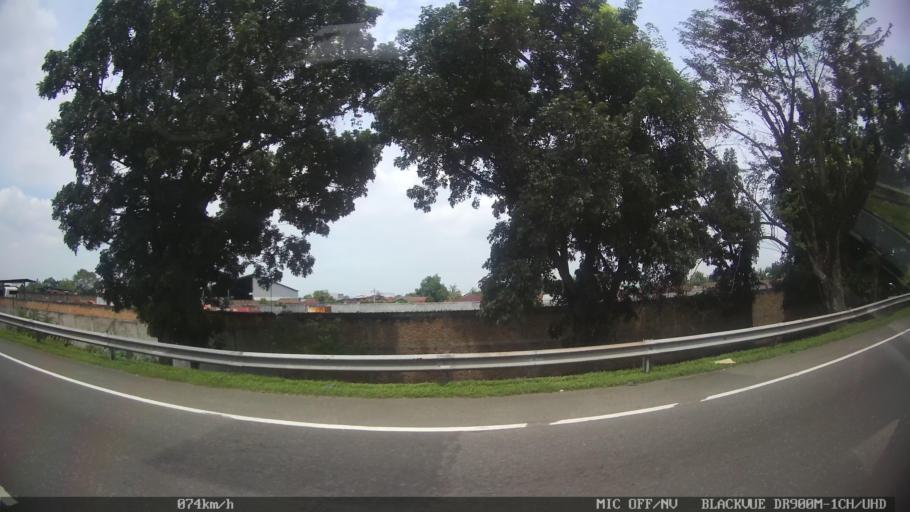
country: ID
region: North Sumatra
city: Labuhan Deli
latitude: 3.6925
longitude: 98.6820
